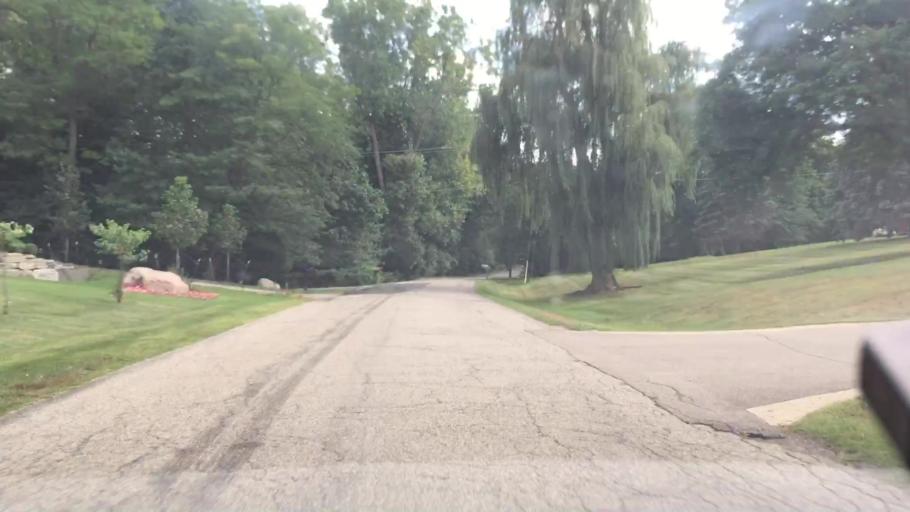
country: US
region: Michigan
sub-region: Oakland County
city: Sylvan Lake
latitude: 42.5679
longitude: -83.3153
